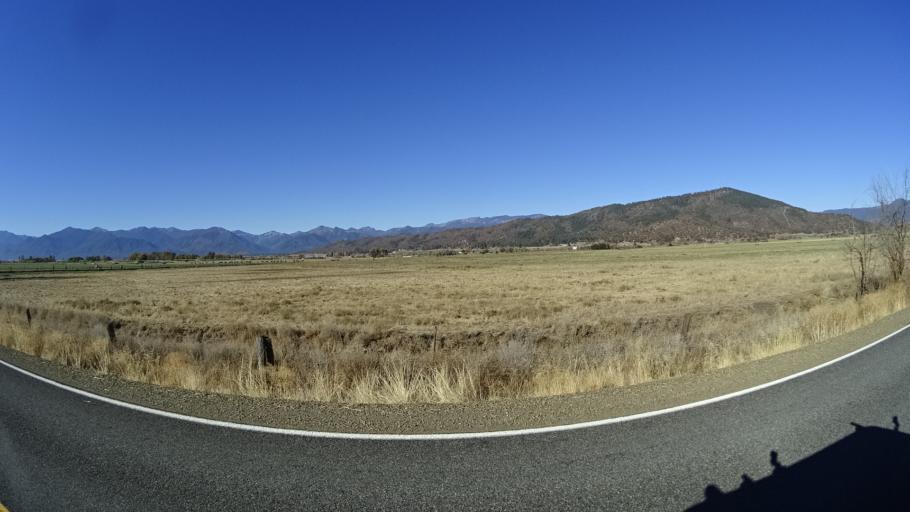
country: US
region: California
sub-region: Siskiyou County
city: Yreka
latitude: 41.5748
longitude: -122.8364
